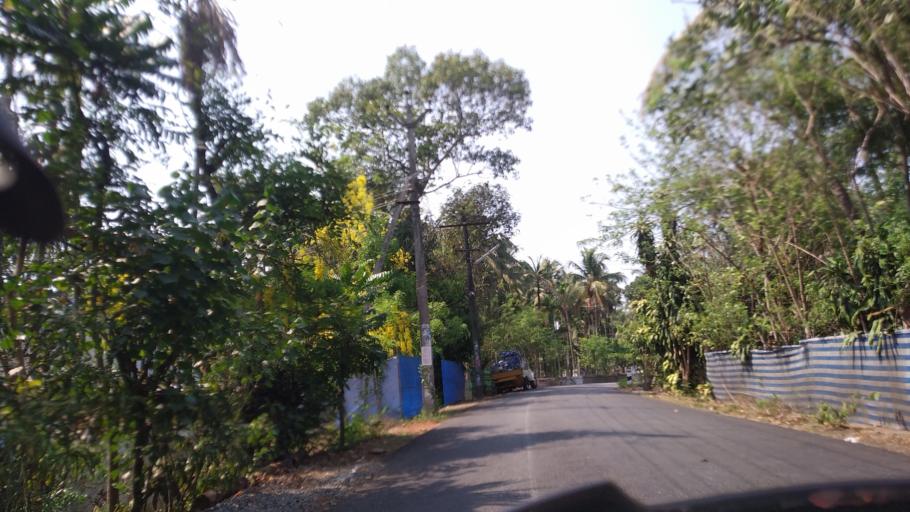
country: IN
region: Kerala
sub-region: Thrissur District
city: Thanniyam
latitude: 10.3601
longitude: 76.1090
